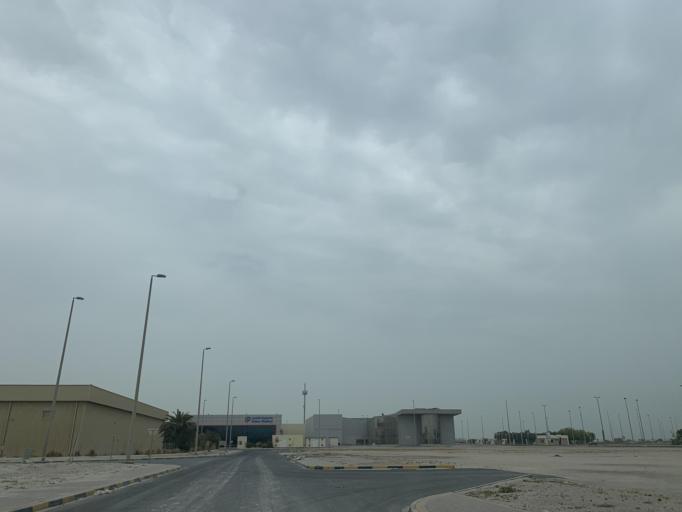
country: BH
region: Muharraq
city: Al Hadd
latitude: 26.2216
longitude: 50.6730
